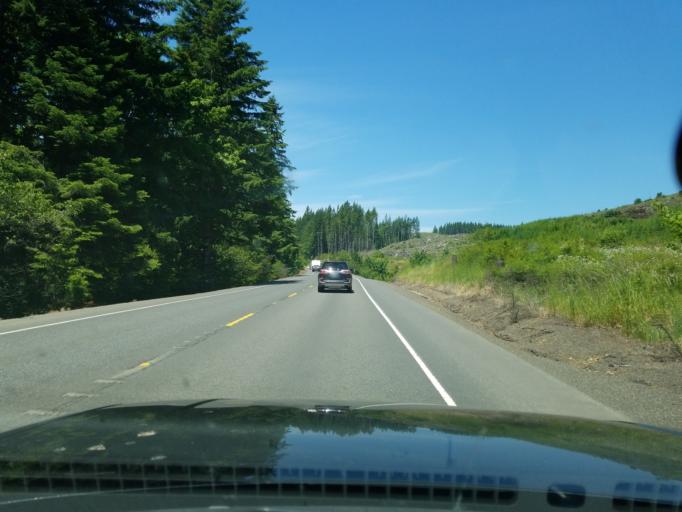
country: US
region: Oregon
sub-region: Columbia County
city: Vernonia
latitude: 45.7692
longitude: -123.3195
